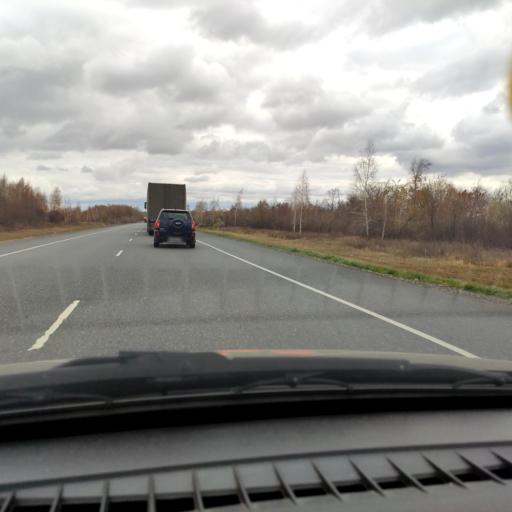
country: RU
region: Samara
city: Mezhdurechensk
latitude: 53.2411
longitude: 48.9705
